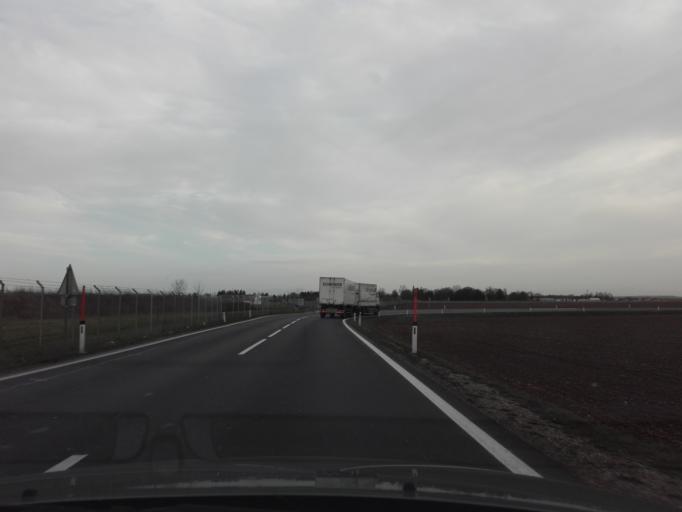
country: AT
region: Upper Austria
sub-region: Politischer Bezirk Linz-Land
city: Horsching
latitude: 48.2383
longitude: 14.1778
